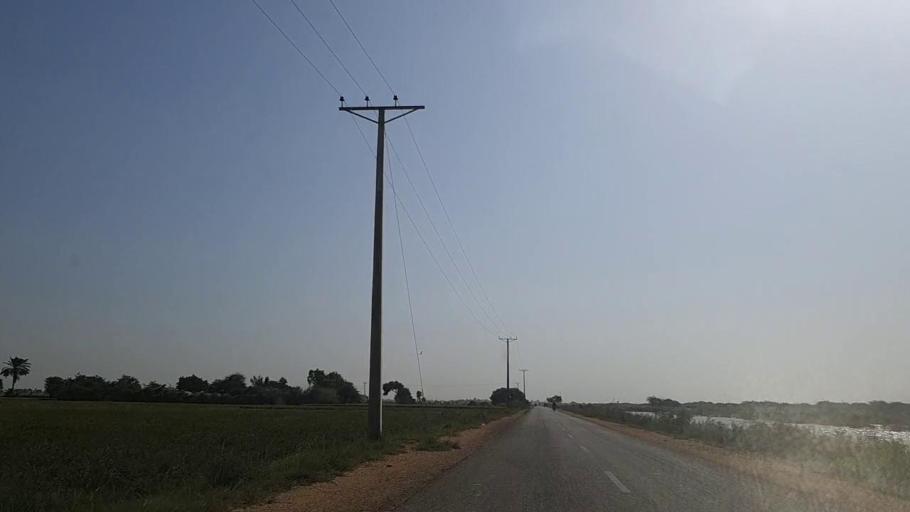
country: PK
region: Sindh
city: Mirpur Batoro
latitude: 24.5416
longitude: 68.2800
